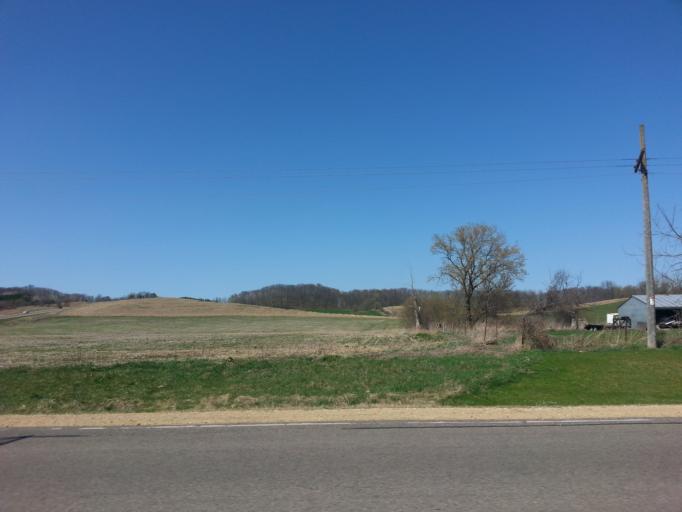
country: US
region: Wisconsin
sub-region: Dunn County
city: Menomonie
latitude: 44.8905
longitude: -91.9641
